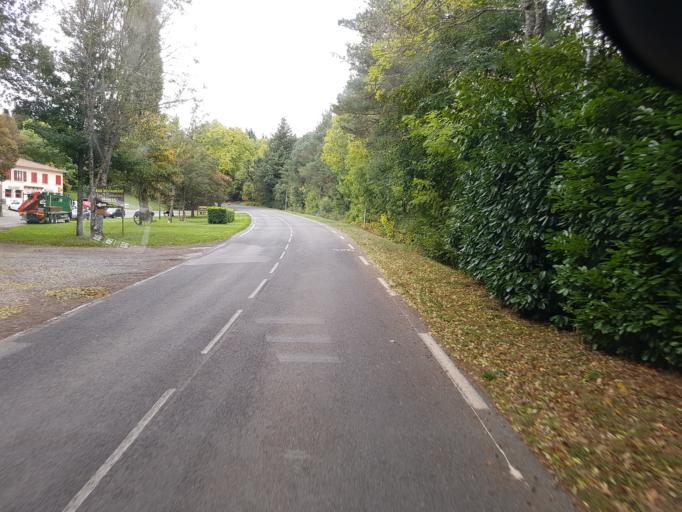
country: FR
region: Languedoc-Roussillon
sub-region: Departement de l'Aude
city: Cuxac-Cabardes
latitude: 43.4166
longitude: 2.3015
